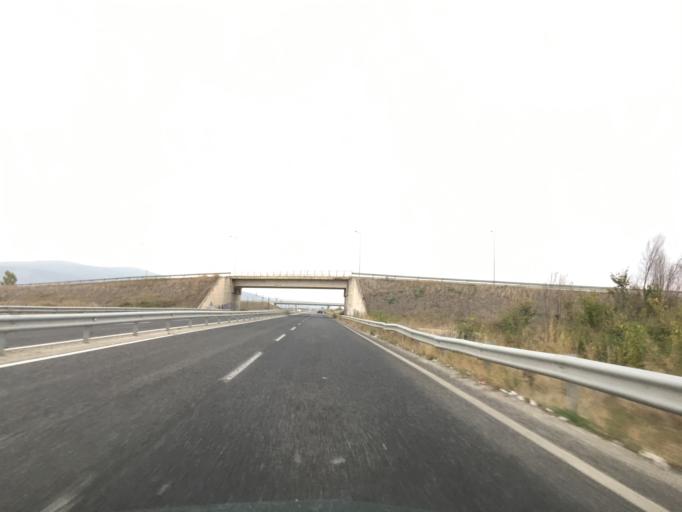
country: GR
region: Thessaly
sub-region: Trikala
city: Megalochori
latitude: 39.5662
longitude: 21.8078
